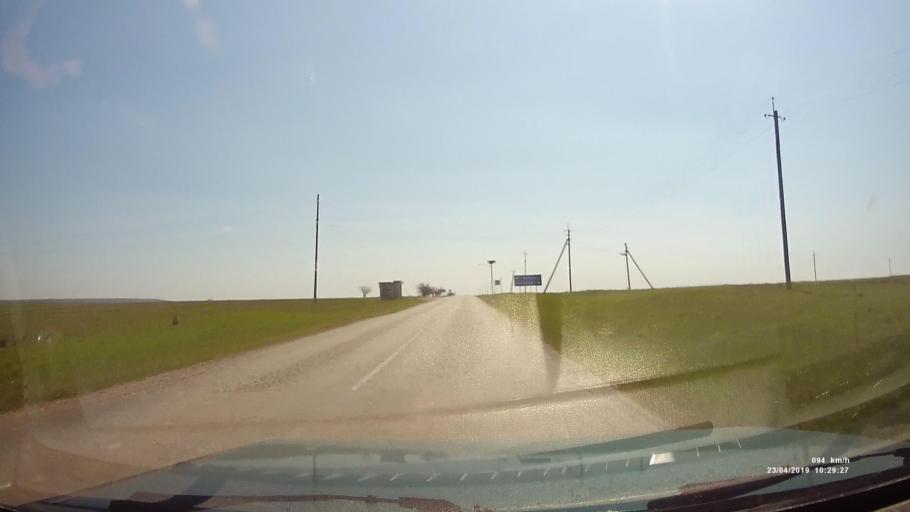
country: RU
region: Kalmykiya
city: Yashalta
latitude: 46.5985
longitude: 42.5267
